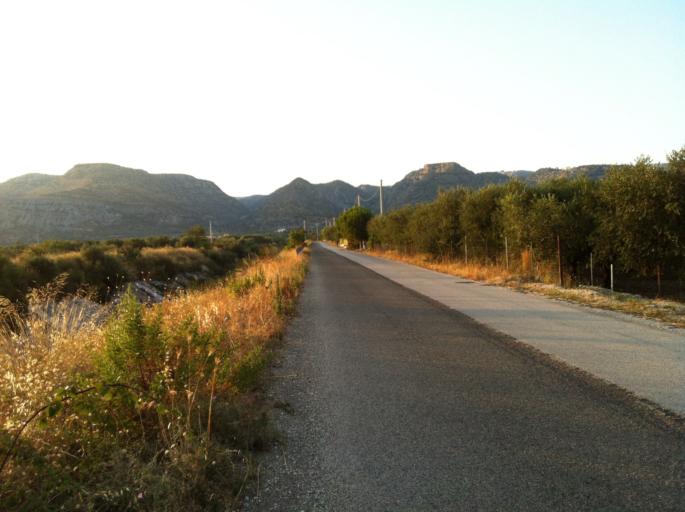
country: IT
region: Apulia
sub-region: Provincia di Foggia
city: Monte Sant'Angelo
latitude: 41.6571
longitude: 15.9513
